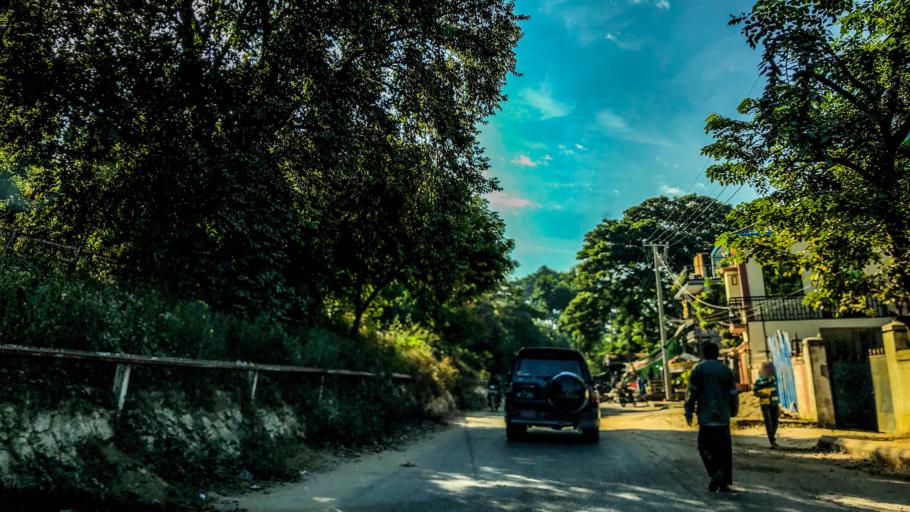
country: MM
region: Sagain
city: Sagaing
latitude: 21.8797
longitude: 95.9856
